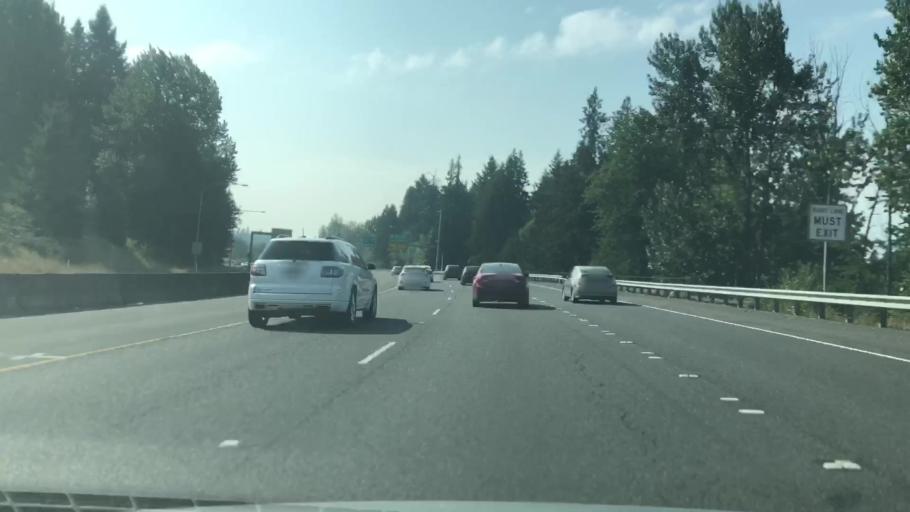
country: US
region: Washington
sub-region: Clark County
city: Minnehaha
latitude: 45.6479
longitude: -122.6437
